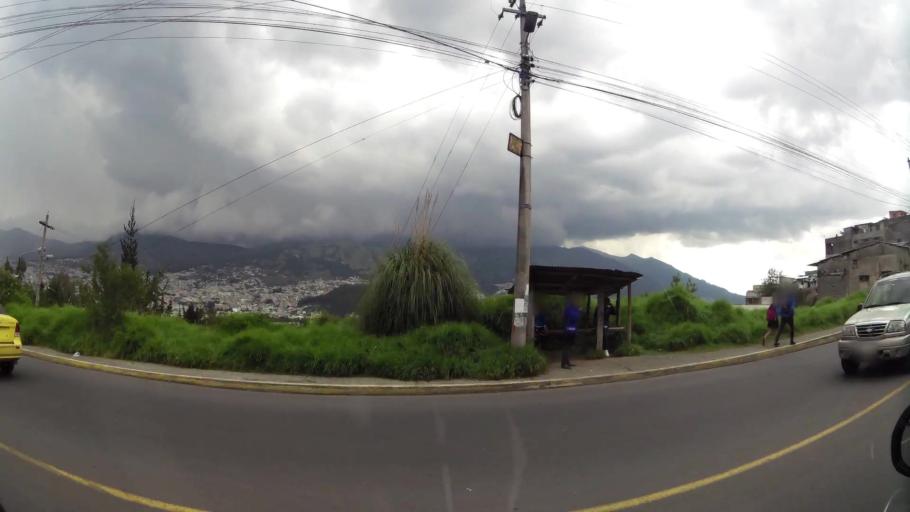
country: EC
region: Pichincha
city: Quito
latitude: -0.2446
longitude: -78.5026
